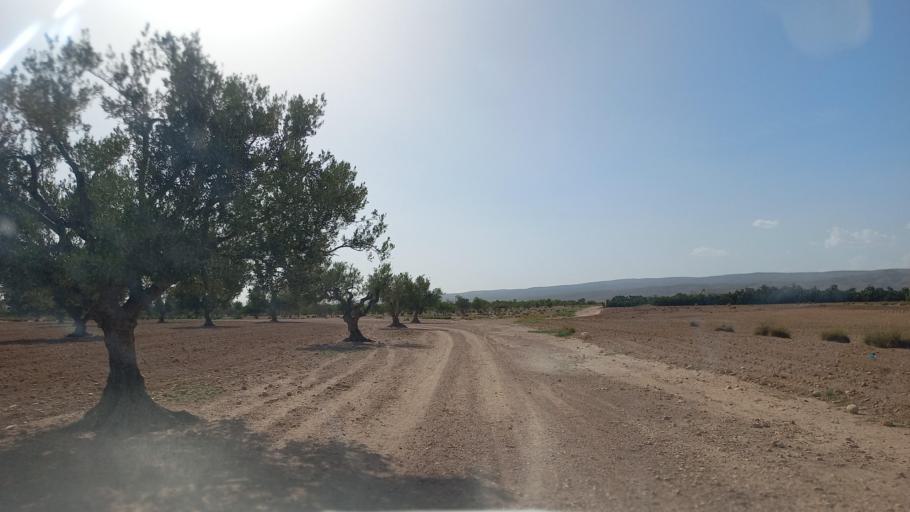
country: TN
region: Al Qasrayn
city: Kasserine
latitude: 35.3136
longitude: 9.0133
